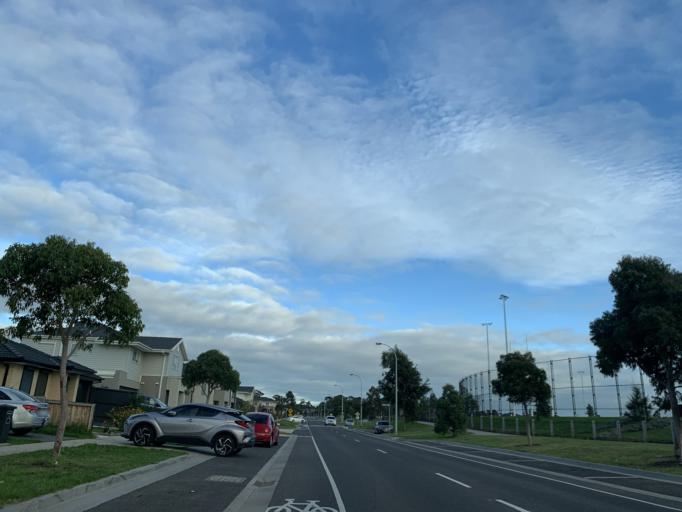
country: AU
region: Victoria
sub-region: Casey
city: Cranbourne East
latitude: -38.1241
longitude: 145.2987
